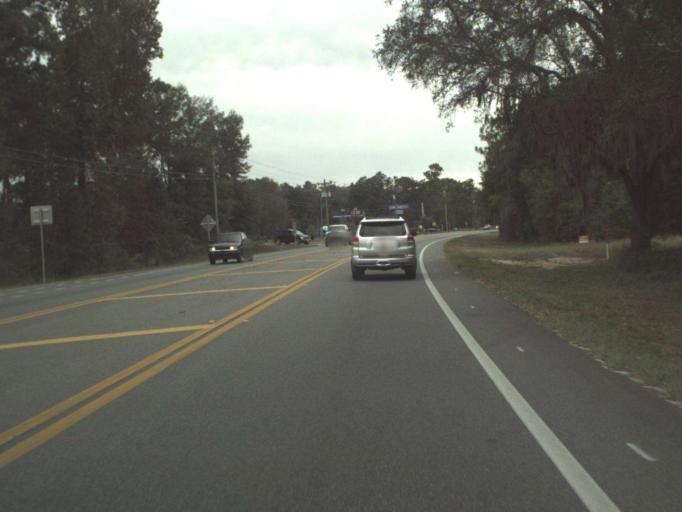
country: US
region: Florida
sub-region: Wakulla County
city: Crawfordville
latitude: 30.2184
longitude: -84.3624
